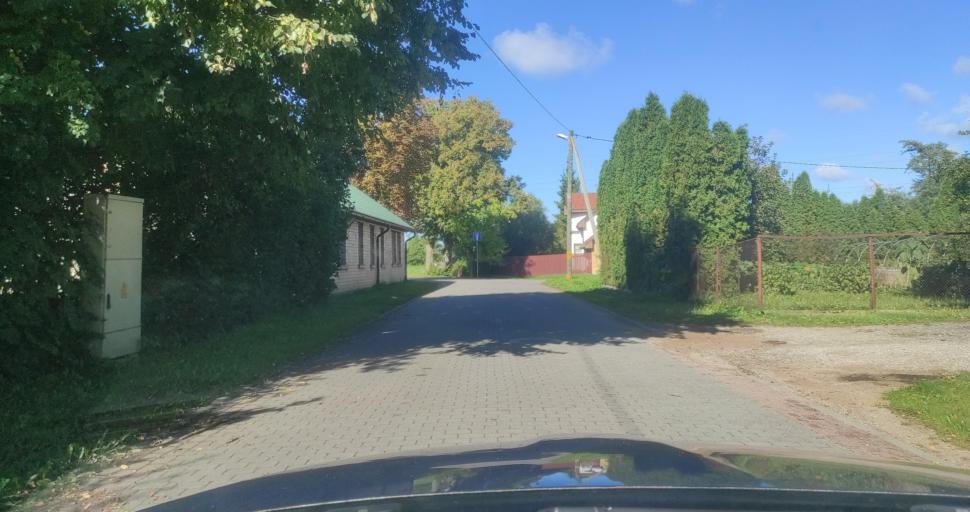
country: LV
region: Ventspils
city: Ventspils
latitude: 57.3855
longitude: 21.6103
